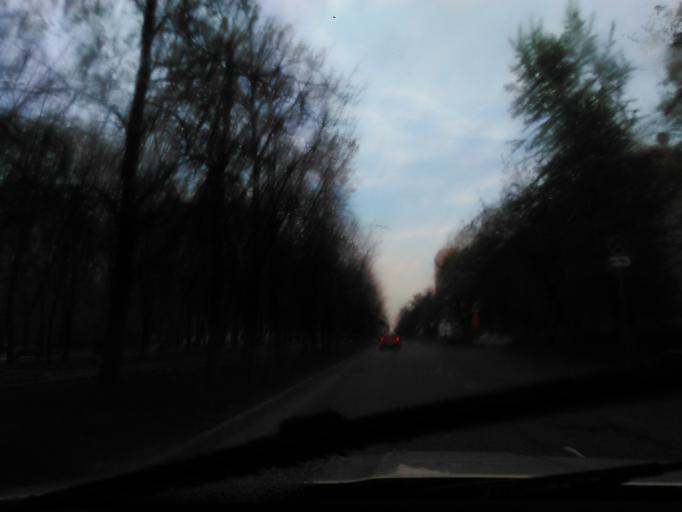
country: RU
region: Moscow
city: Tekstil'shchiki
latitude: 55.7059
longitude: 37.7466
